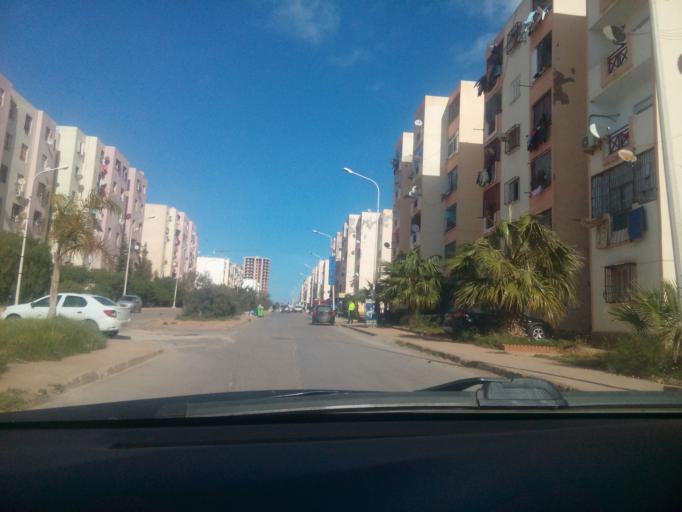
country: DZ
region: Oran
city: Bir el Djir
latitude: 35.7038
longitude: -0.5640
